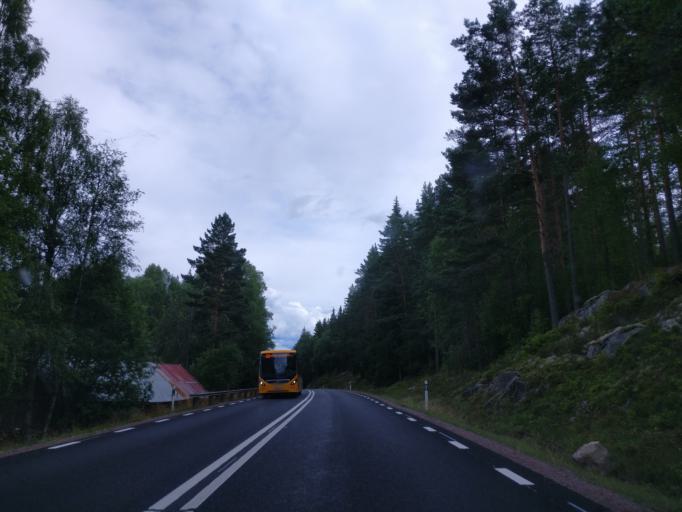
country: SE
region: Vaermland
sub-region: Hagfors Kommun
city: Hagfors
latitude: 60.0562
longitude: 13.5552
